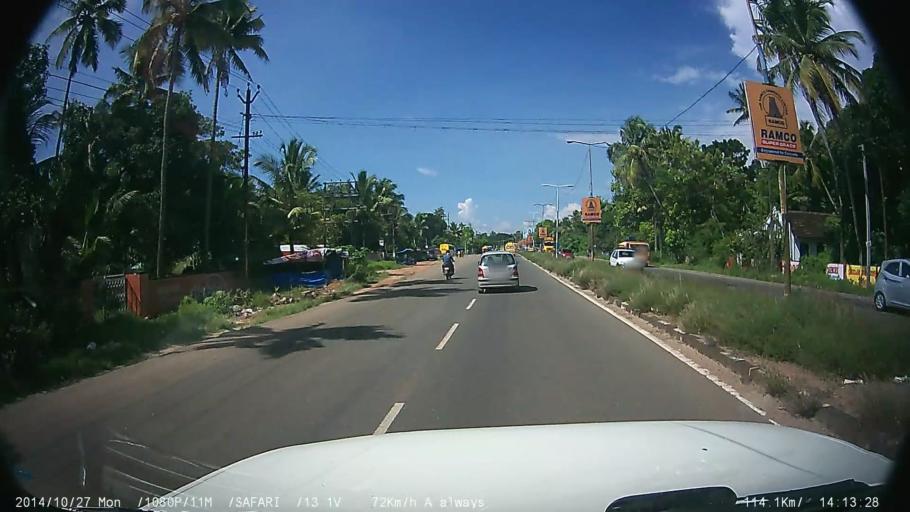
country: IN
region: Kerala
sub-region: Alappuzha
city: Kutiatodu
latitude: 9.8137
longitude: 76.3136
